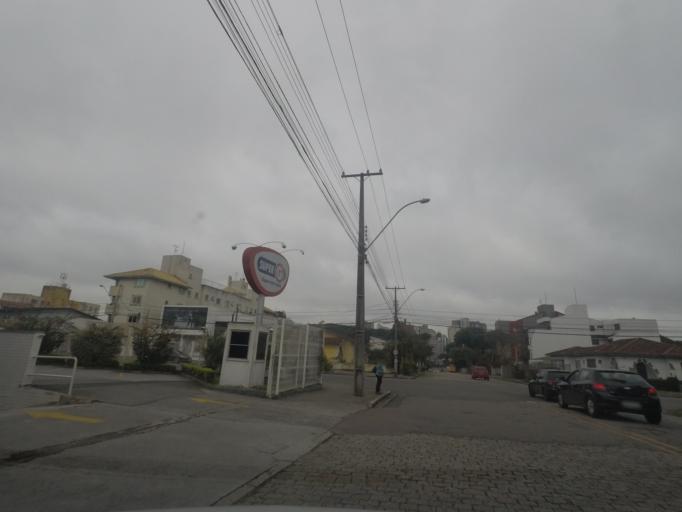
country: BR
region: Parana
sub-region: Curitiba
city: Curitiba
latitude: -25.4394
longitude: -49.2484
